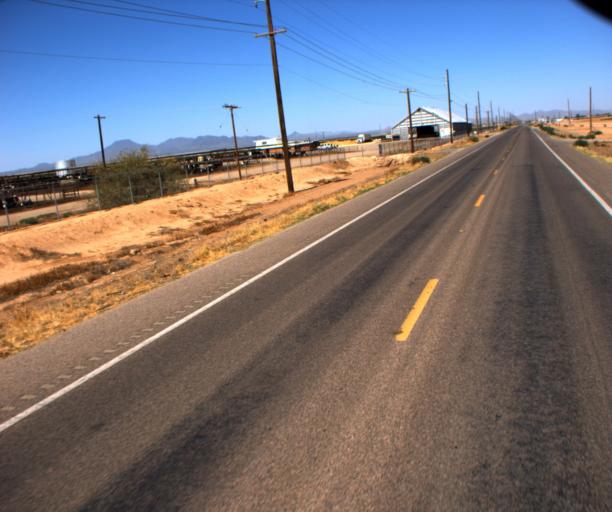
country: US
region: Arizona
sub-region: Pinal County
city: Casa Grande
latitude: 32.8794
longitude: -111.9199
